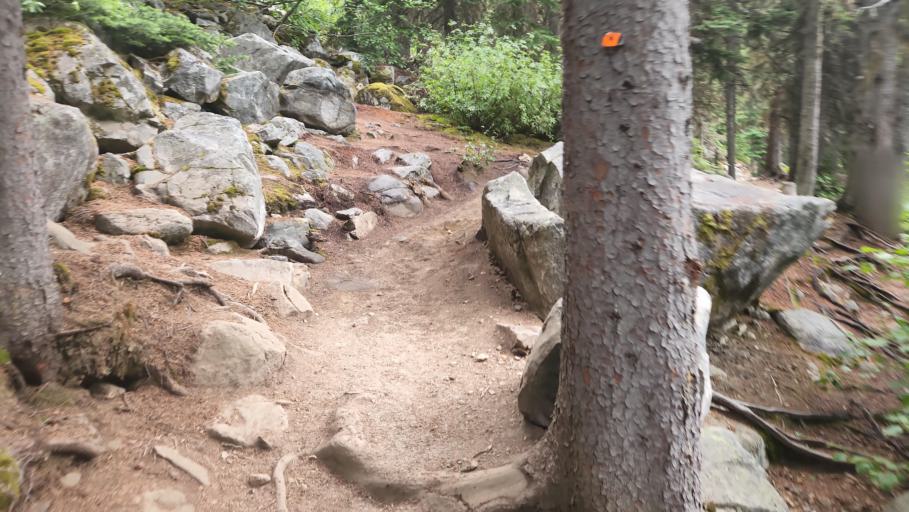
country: CA
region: British Columbia
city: Pemberton
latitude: 50.3524
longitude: -122.4821
